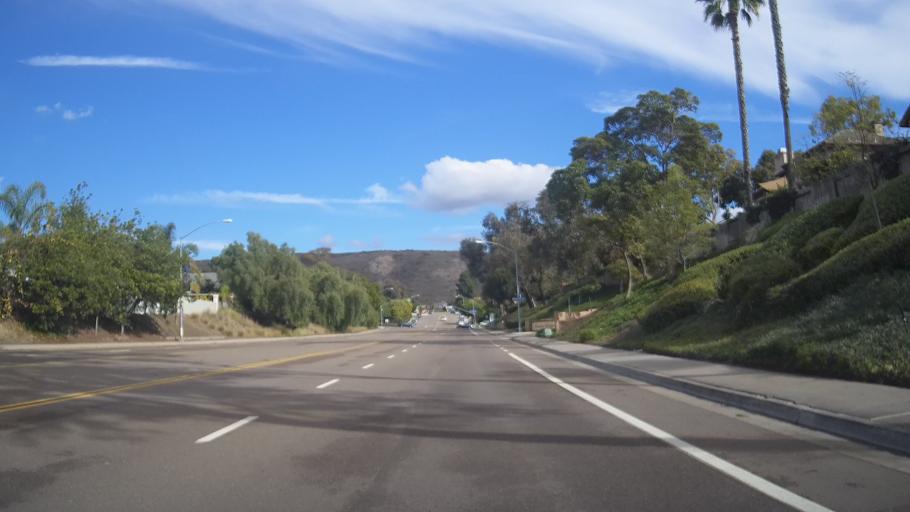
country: US
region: California
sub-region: San Diego County
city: Fairbanks Ranch
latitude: 32.9613
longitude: -117.1201
